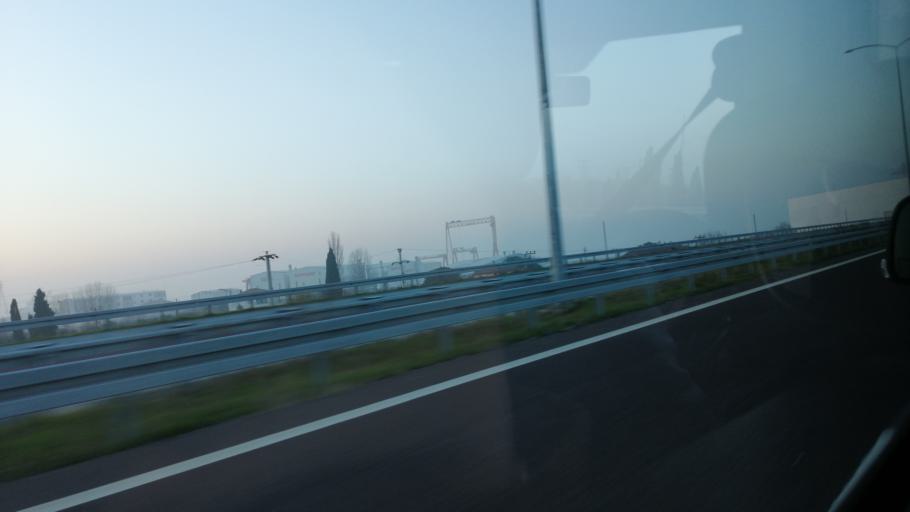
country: TR
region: Yalova
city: Altinova
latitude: 40.7224
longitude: 29.5029
